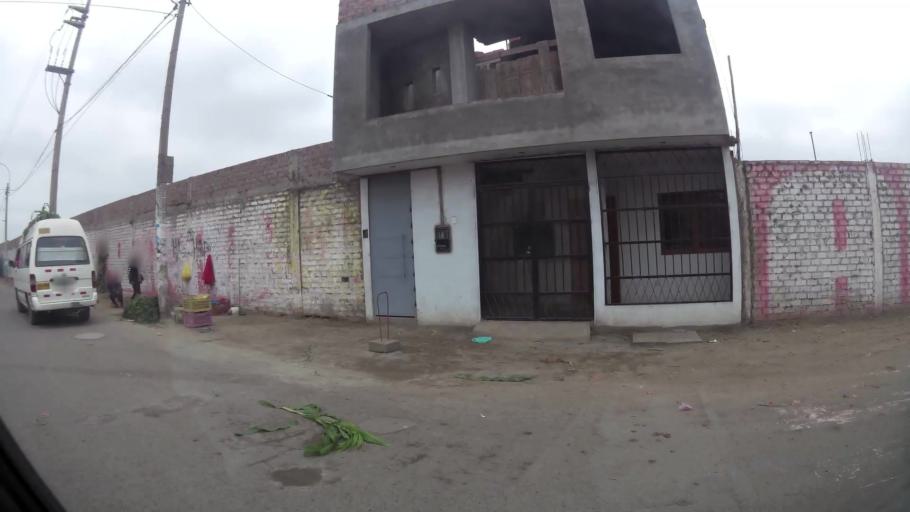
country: PE
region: Lima
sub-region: Provincia de Huaral
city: Huaral
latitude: -11.5029
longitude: -77.2053
